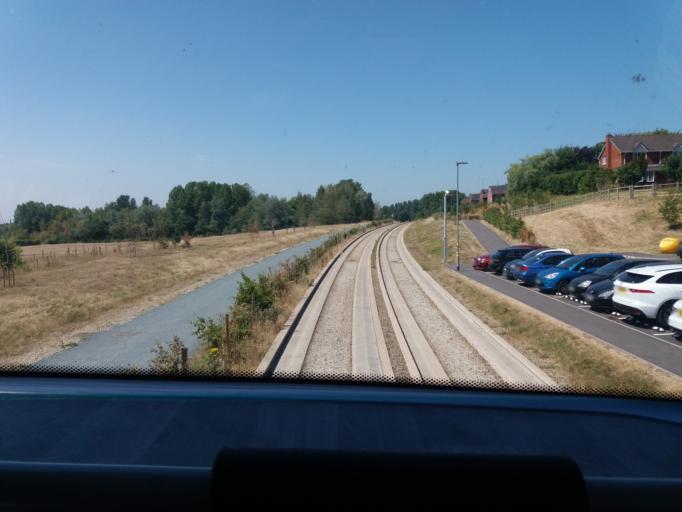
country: GB
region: England
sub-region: Borough of Wigan
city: Tyldesley
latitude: 53.5125
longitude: -2.4680
